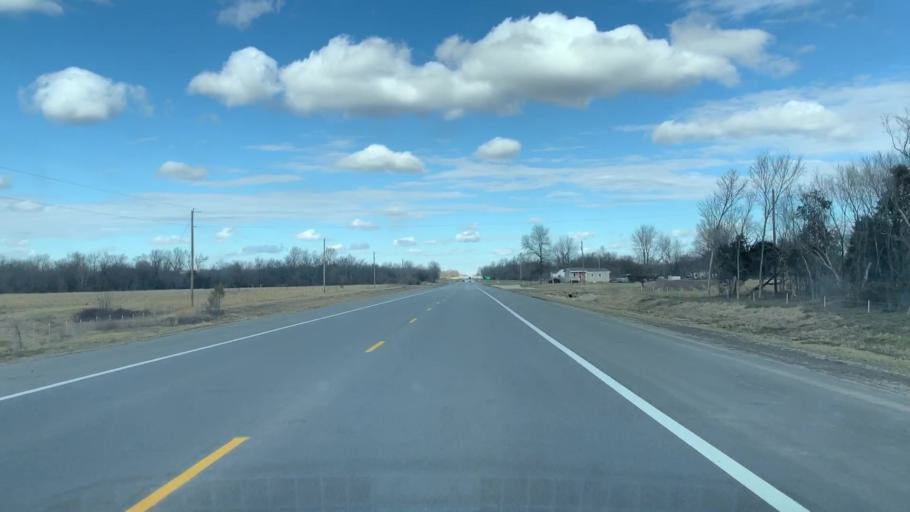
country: US
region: Kansas
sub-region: Cherokee County
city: Columbus
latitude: 37.2706
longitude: -94.8321
